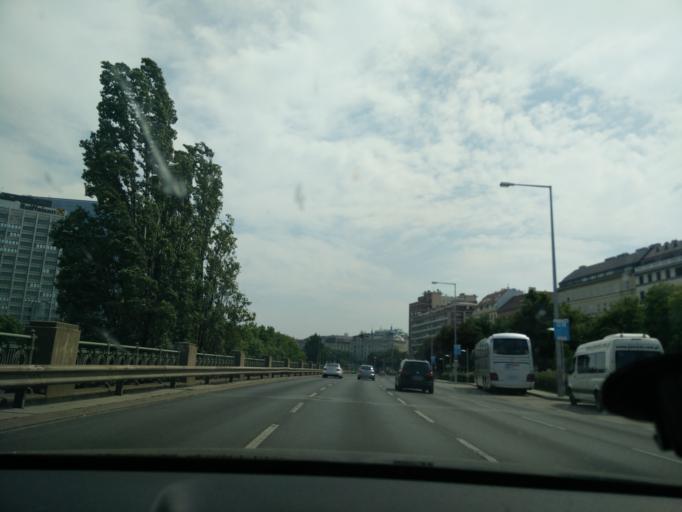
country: AT
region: Vienna
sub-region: Wien Stadt
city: Vienna
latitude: 48.2159
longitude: 16.3731
